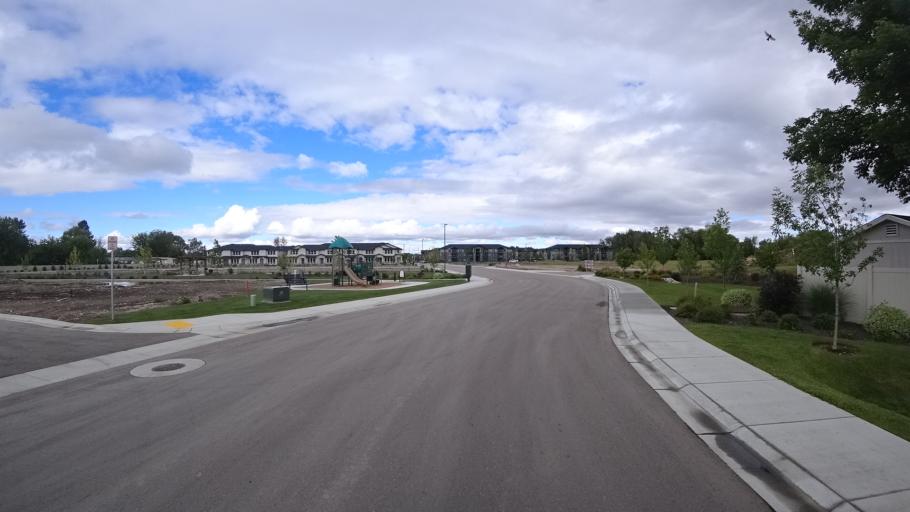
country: US
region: Idaho
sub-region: Ada County
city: Eagle
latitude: 43.6754
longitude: -116.2866
